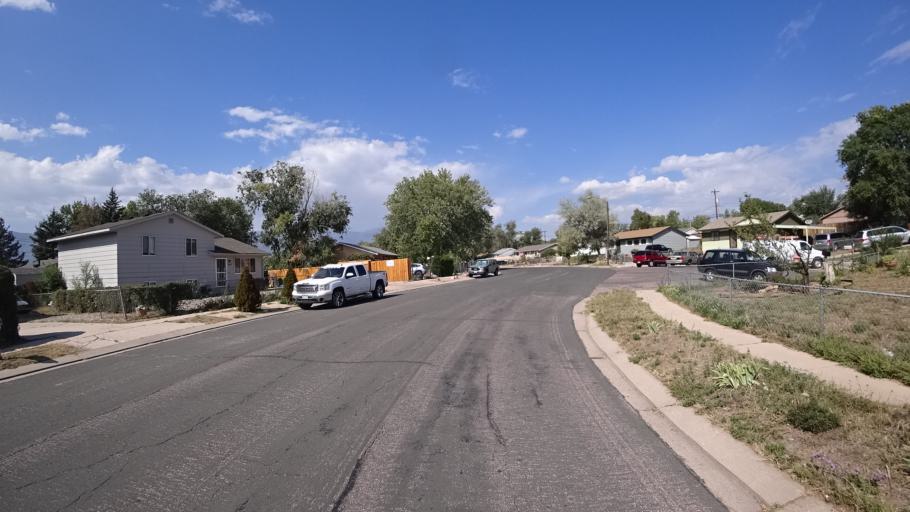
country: US
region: Colorado
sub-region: El Paso County
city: Colorado Springs
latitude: 38.8211
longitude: -104.7843
